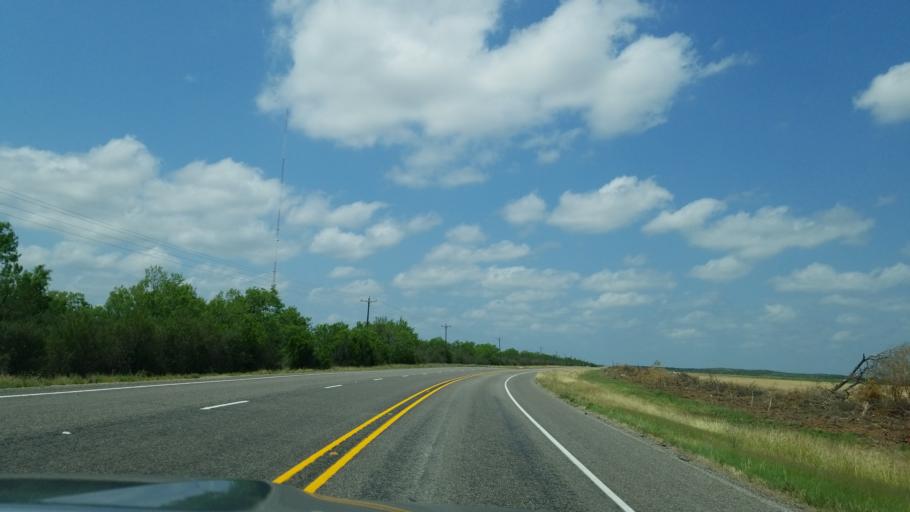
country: US
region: Texas
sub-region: Frio County
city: Pearsall
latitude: 28.9465
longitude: -99.2732
